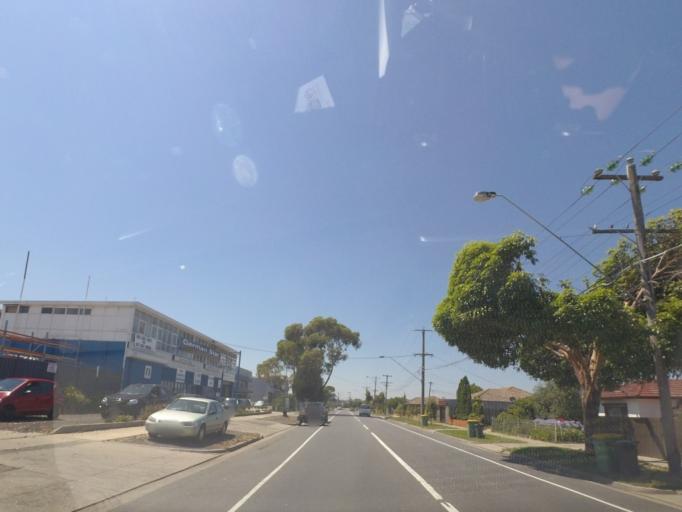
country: AU
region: Victoria
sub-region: Darebin
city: Reservoir
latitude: -37.7093
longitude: 144.9899
